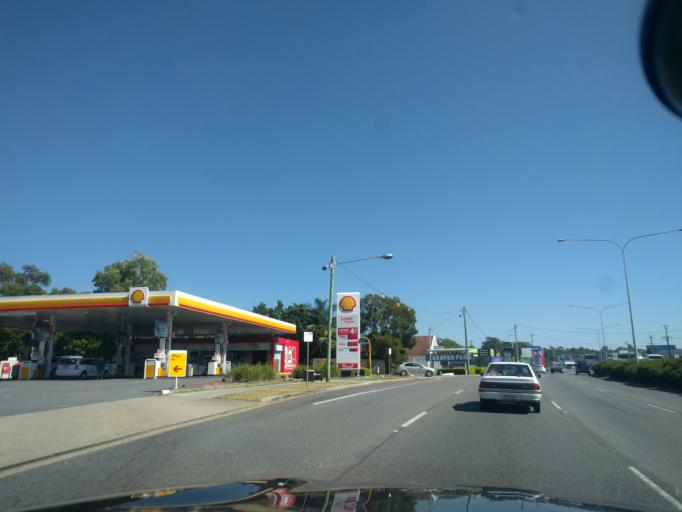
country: AU
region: Queensland
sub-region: Brisbane
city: Bridegman Downs
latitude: -27.3601
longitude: 153.0167
